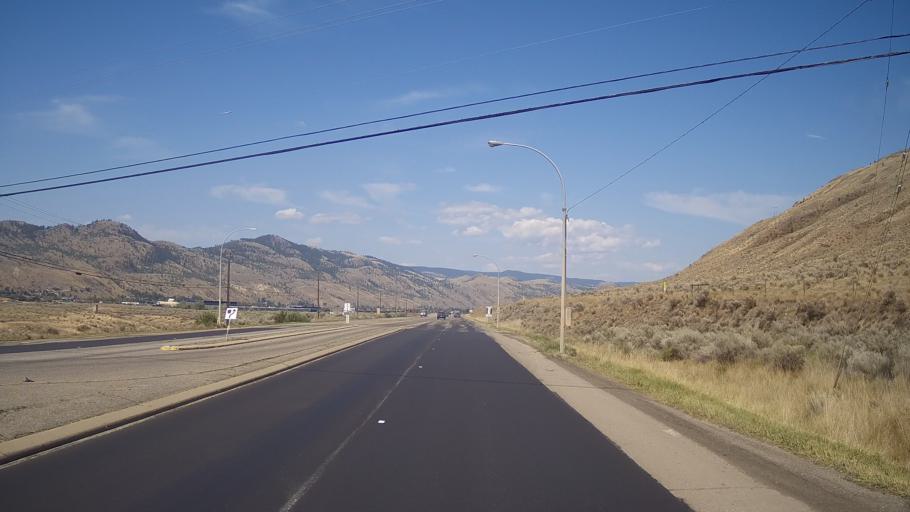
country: CA
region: British Columbia
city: Kamloops
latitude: 50.7222
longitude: -120.3348
